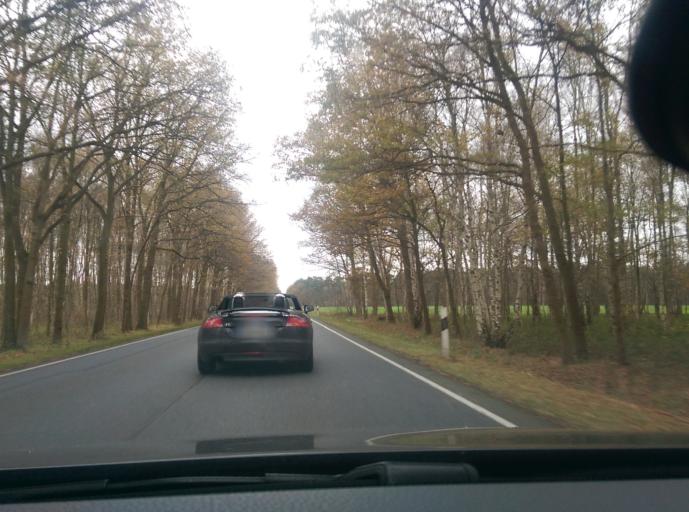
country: DE
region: Lower Saxony
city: Wietze
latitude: 52.5779
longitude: 9.8672
